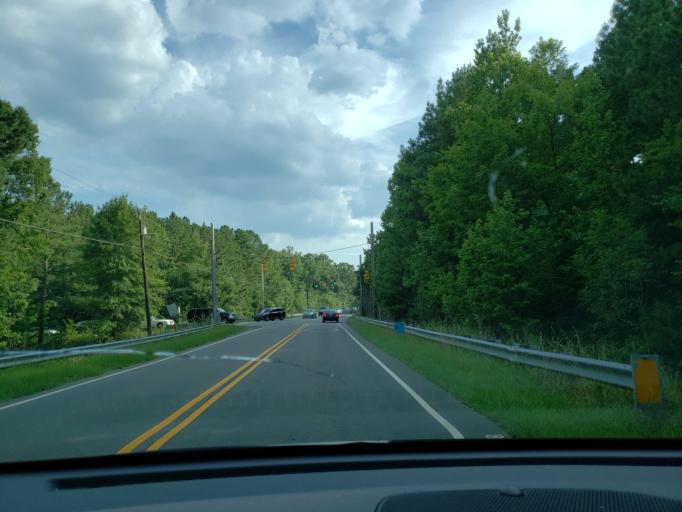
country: US
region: North Carolina
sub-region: Orange County
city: Chapel Hill
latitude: 35.8890
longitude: -78.9827
